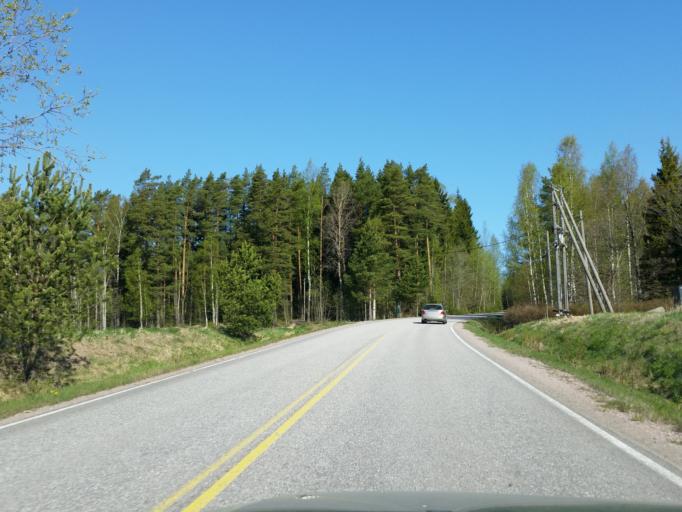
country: FI
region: Uusimaa
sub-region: Helsinki
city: Kirkkonummi
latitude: 60.1888
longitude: 24.3963
